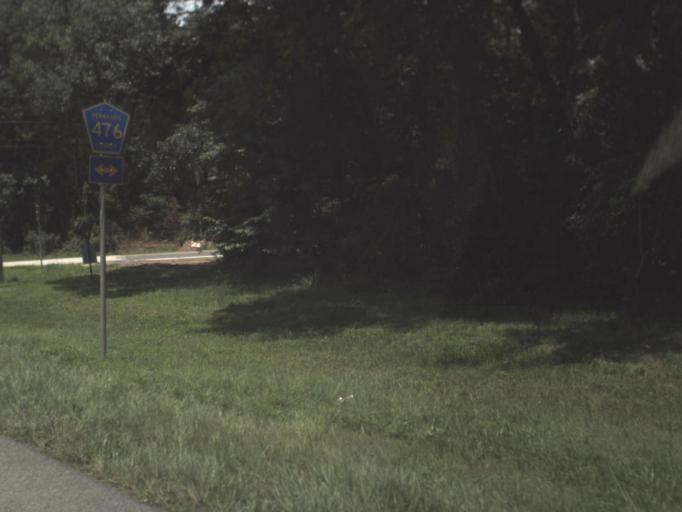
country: US
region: Florida
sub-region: Hernando County
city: North Brooksville
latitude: 28.6287
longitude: -82.4226
